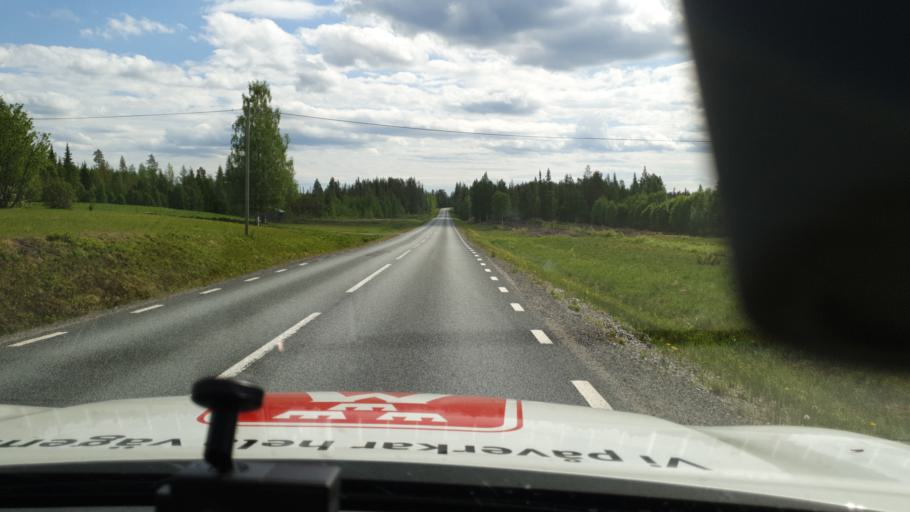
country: SE
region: Vaesterbotten
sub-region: Sorsele Kommun
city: Sorsele
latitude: 65.3894
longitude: 17.5746
